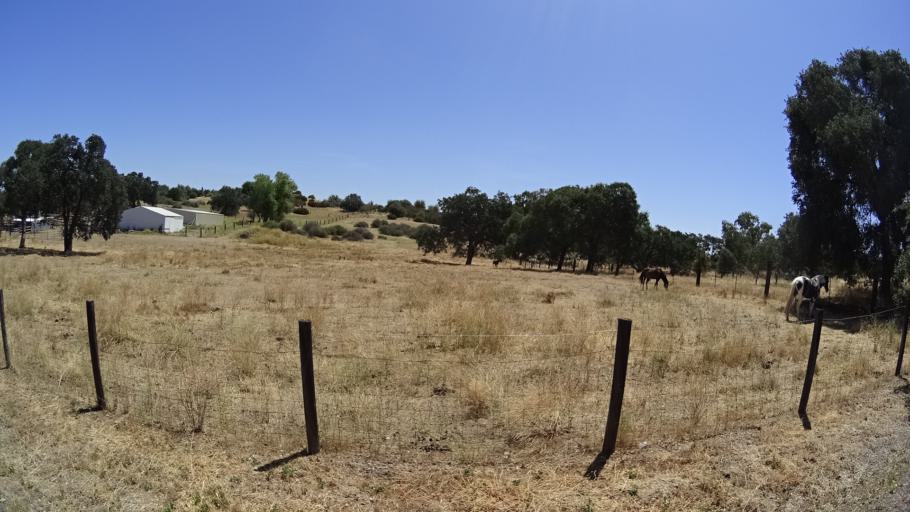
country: US
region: California
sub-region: Calaveras County
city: Rancho Calaveras
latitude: 38.1467
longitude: -120.9448
